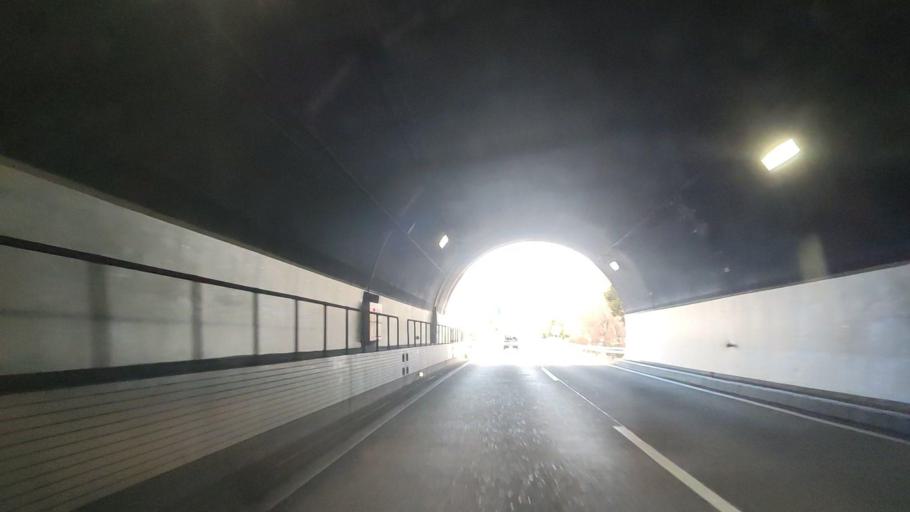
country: JP
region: Hyogo
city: Kariya
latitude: 34.7876
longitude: 134.1487
